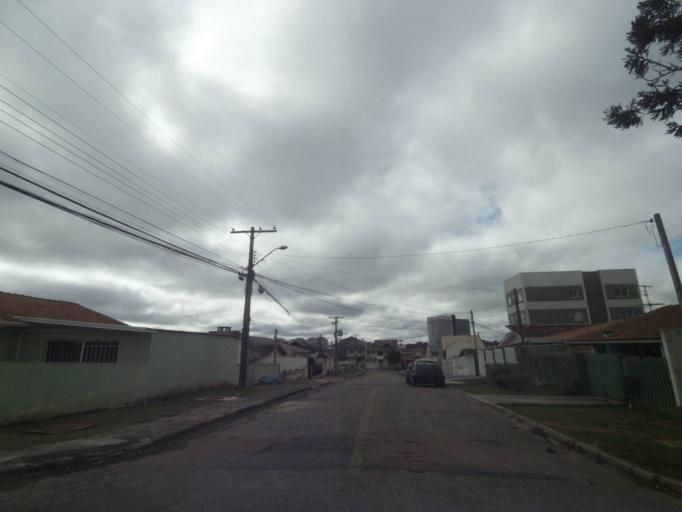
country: BR
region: Parana
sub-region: Curitiba
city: Curitiba
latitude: -25.4981
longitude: -49.2834
